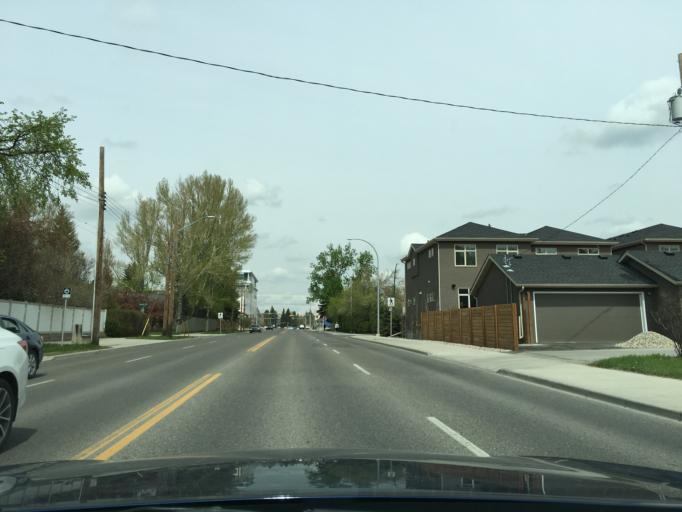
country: CA
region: Alberta
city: Calgary
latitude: 51.0063
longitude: -114.0812
